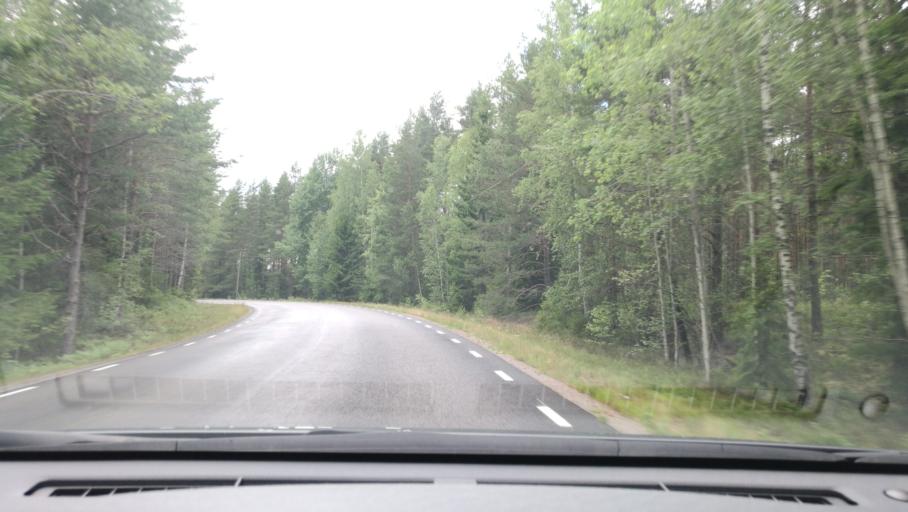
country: SE
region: OEstergoetland
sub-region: Norrkopings Kommun
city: Svartinge
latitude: 58.8181
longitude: 16.0233
